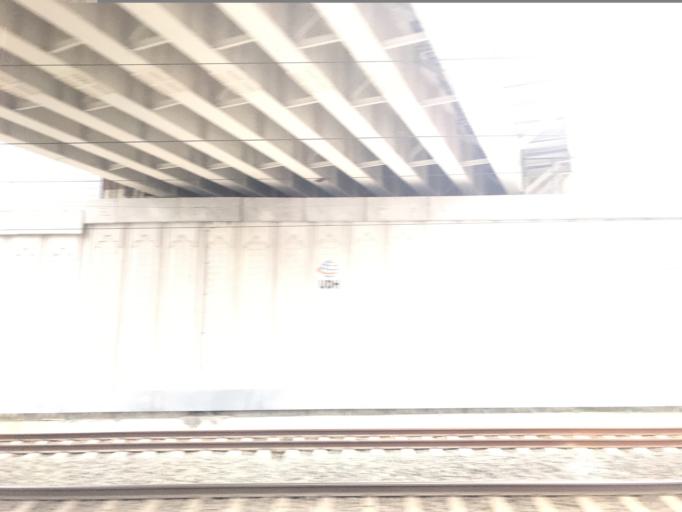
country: TR
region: Istanbul
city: Pendik
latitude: 40.8573
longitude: 29.2777
